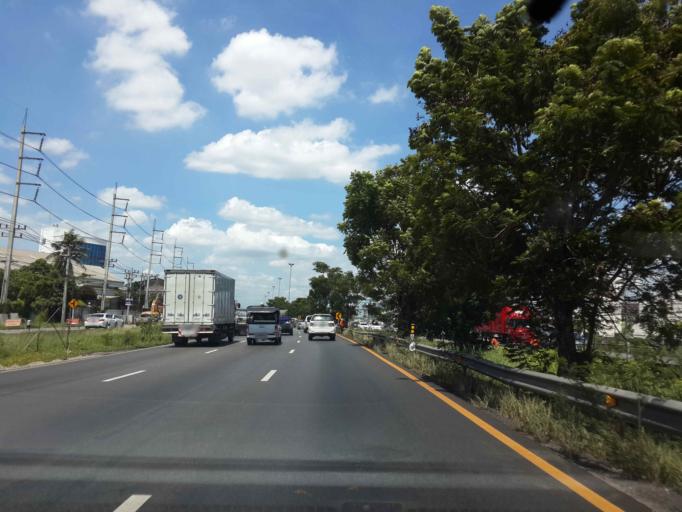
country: TH
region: Bangkok
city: Bang Bon
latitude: 13.5942
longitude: 100.3617
